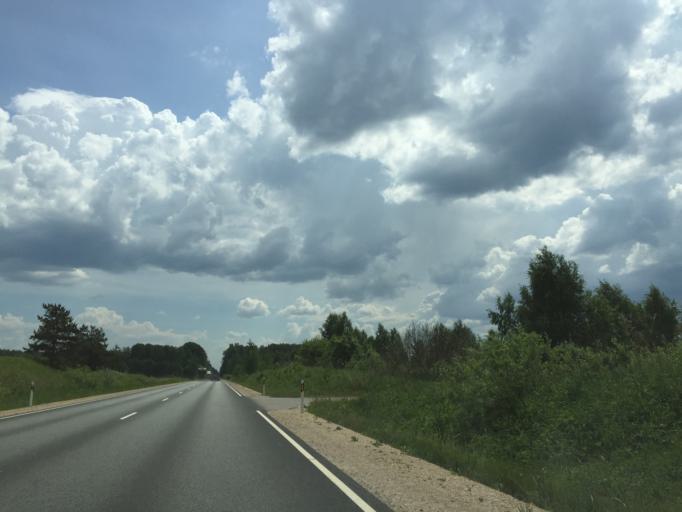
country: LV
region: Ikskile
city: Ikskile
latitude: 56.8836
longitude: 24.5014
